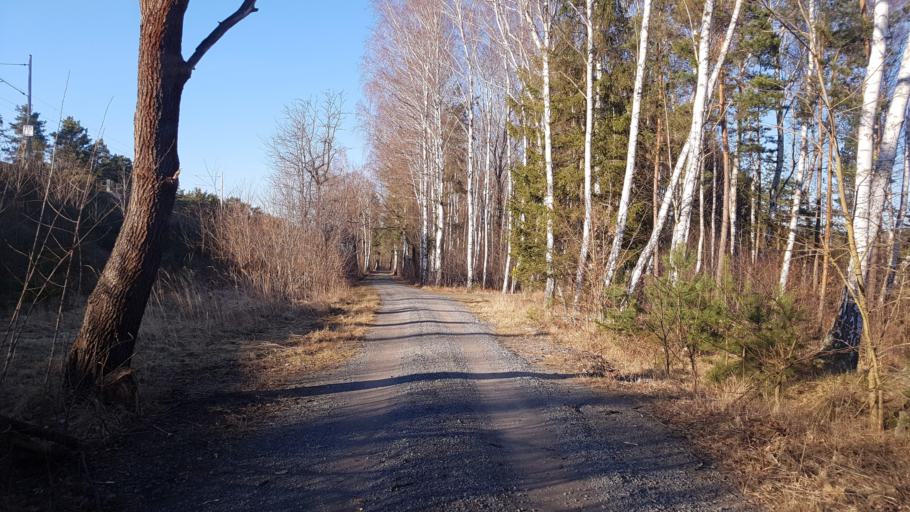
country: DE
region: Brandenburg
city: Hohenleipisch
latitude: 51.5101
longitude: 13.5768
